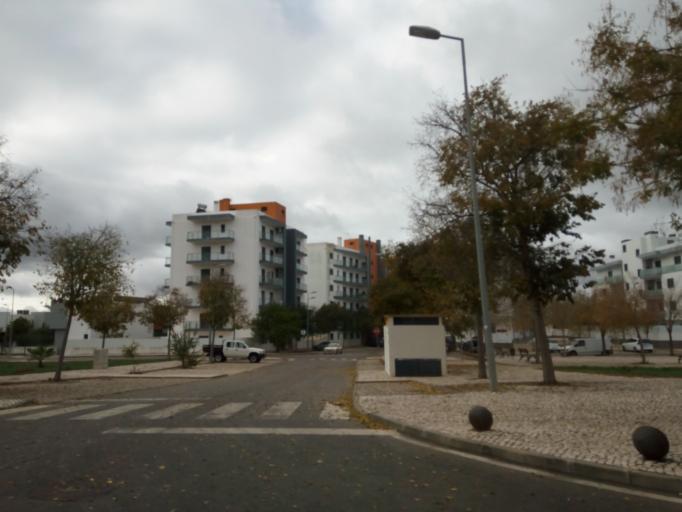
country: PT
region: Faro
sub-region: Loule
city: Loule
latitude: 37.1326
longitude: -8.0082
